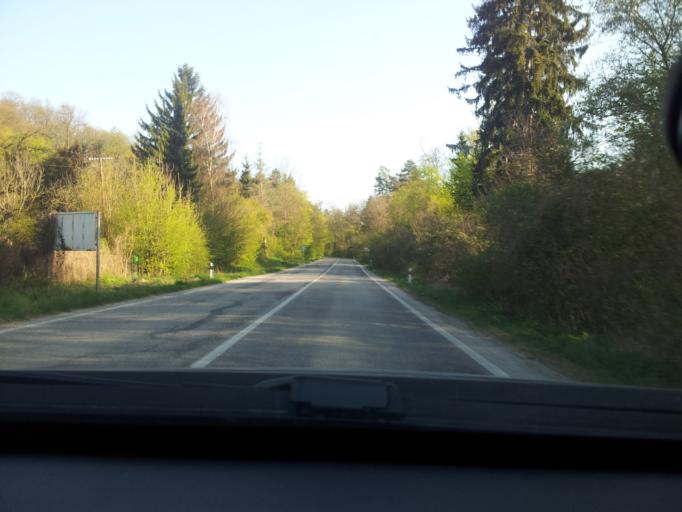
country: SK
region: Nitriansky
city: Zlate Moravce
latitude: 48.4338
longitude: 18.4114
